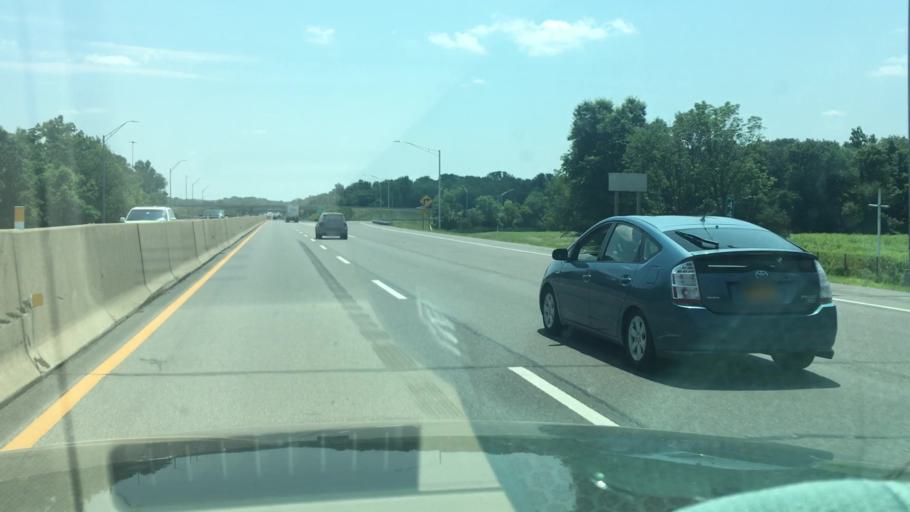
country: US
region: Pennsylvania
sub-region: Bucks County
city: Spinnerstown
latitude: 40.4414
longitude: -75.4288
